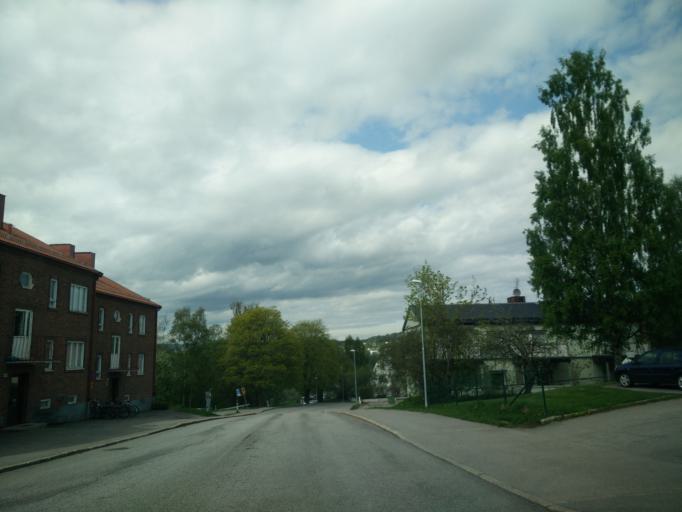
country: SE
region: Vaesternorrland
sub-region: Sundsvalls Kommun
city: Sundsvall
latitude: 62.3856
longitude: 17.2829
